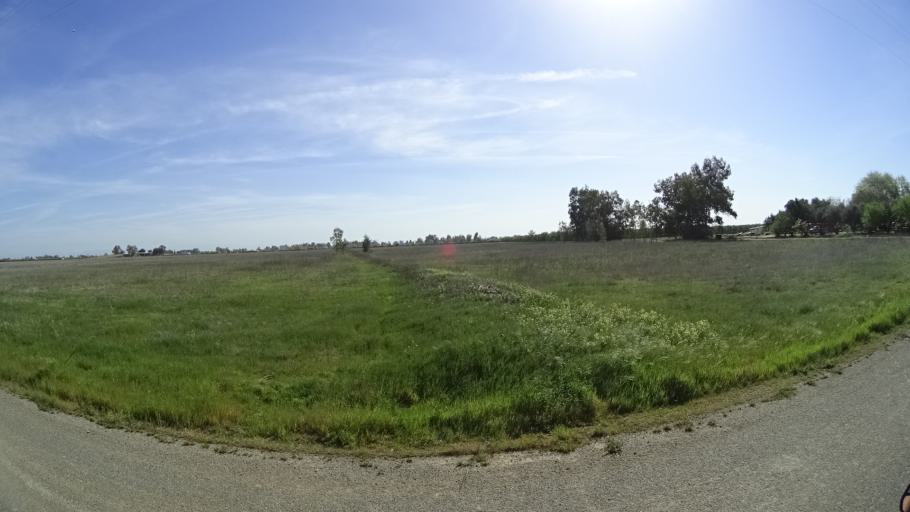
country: US
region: California
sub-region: Glenn County
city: Willows
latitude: 39.6194
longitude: -122.2132
